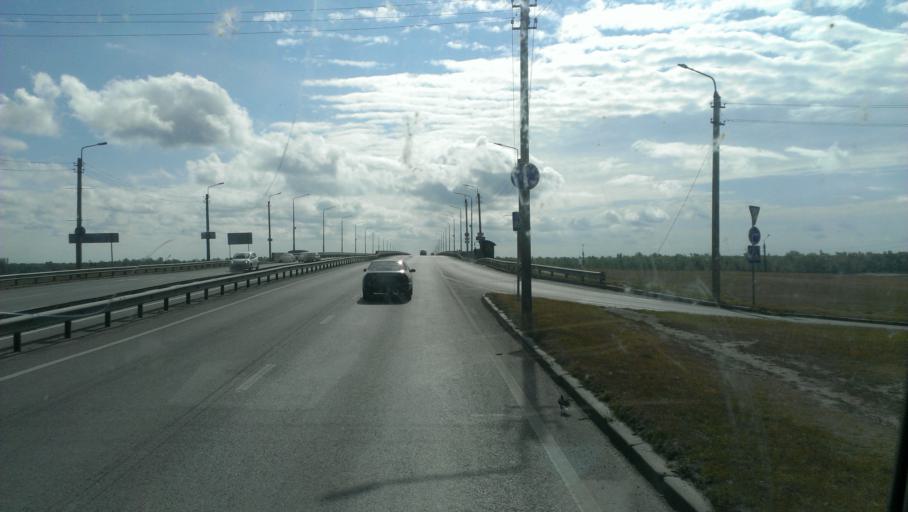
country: RU
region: Altai Krai
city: Zaton
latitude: 53.3254
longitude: 83.7974
